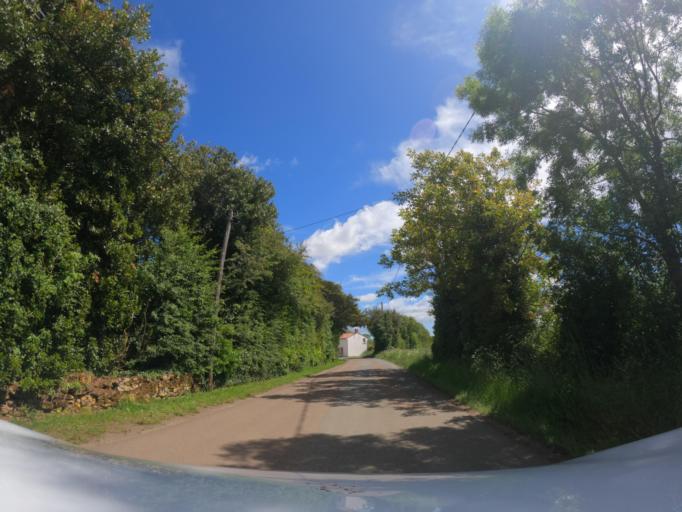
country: FR
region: Pays de la Loire
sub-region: Departement de la Vendee
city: Le Champ-Saint-Pere
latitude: 46.4909
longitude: -1.3267
